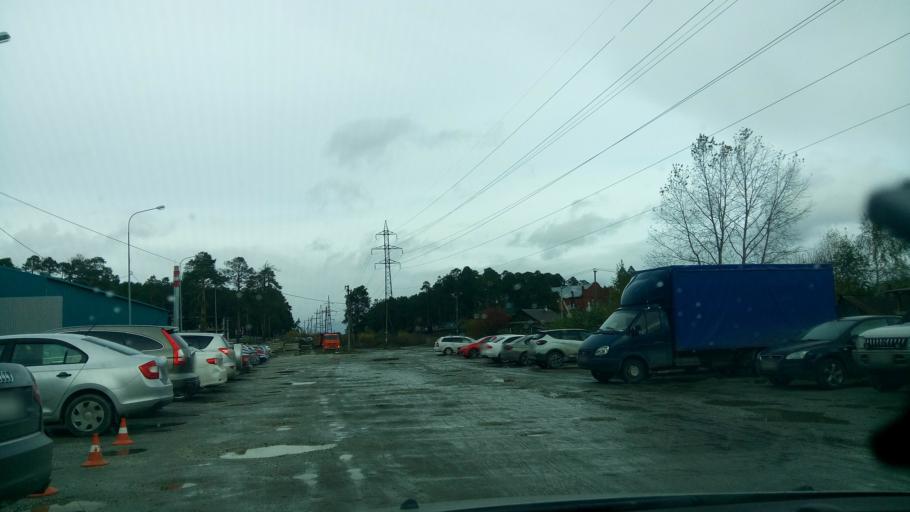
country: RU
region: Sverdlovsk
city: Shirokaya Rechka
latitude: 56.8199
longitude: 60.5220
